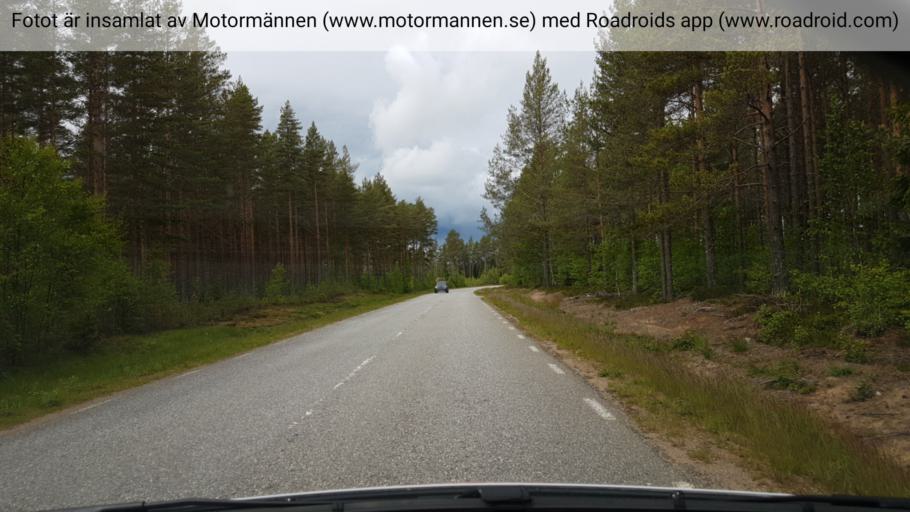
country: SE
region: Vaesterbotten
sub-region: Umea Kommun
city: Hoernefors
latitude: 63.5618
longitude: 19.7142
